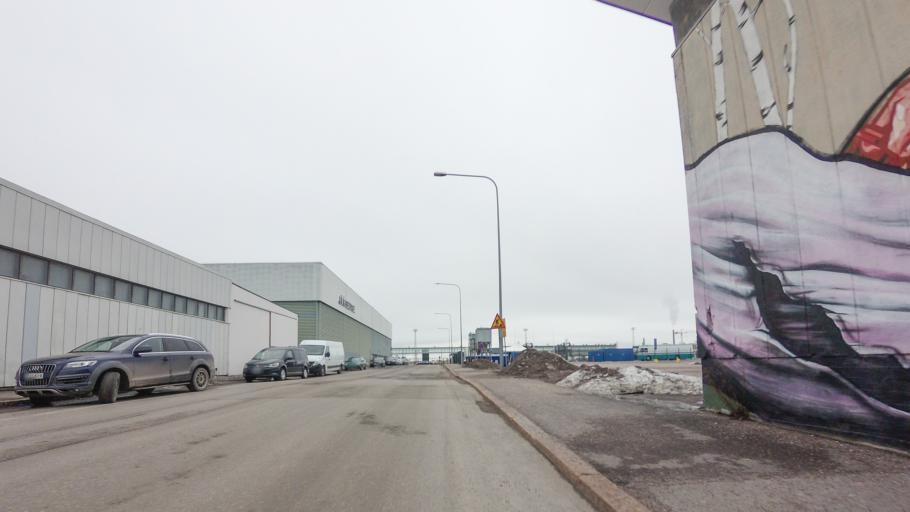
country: FI
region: Uusimaa
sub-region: Helsinki
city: Helsinki
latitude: 60.1490
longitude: 24.9230
